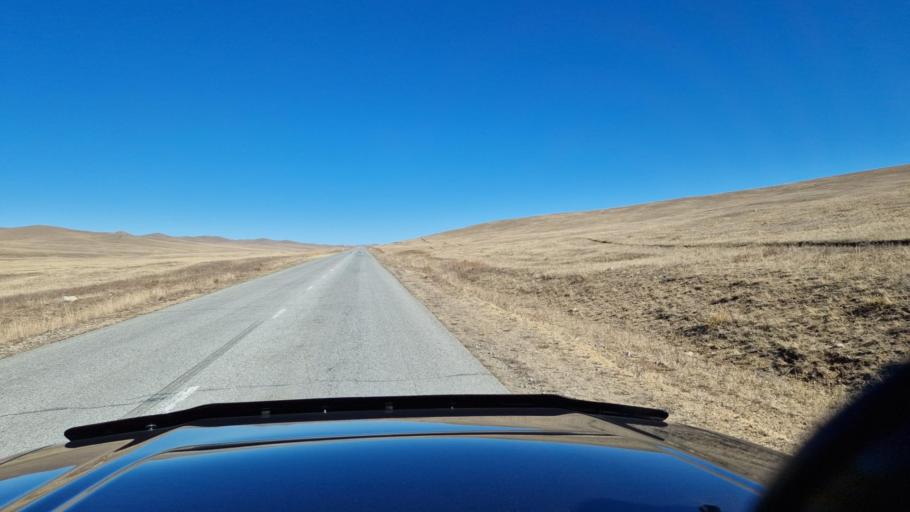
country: MN
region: Hentiy
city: Modot
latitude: 47.7304
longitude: 108.5924
